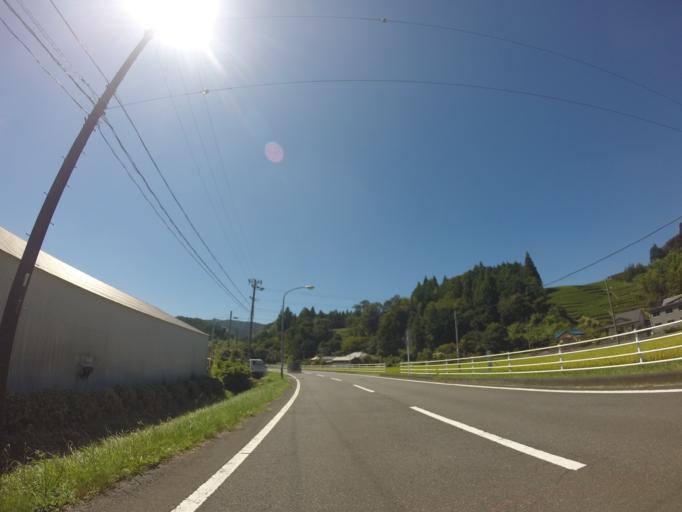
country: JP
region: Shizuoka
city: Fujieda
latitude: 34.9113
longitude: 138.1981
